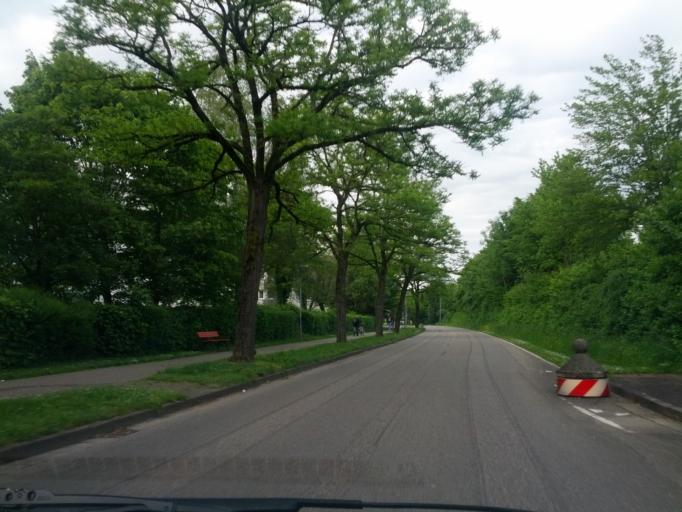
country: DE
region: Baden-Wuerttemberg
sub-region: Freiburg Region
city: Heuweiler
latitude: 48.0707
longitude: 7.9079
